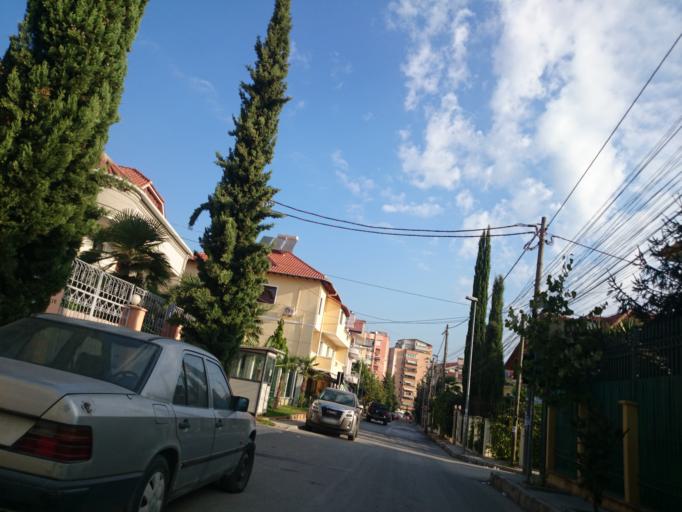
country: AL
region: Tirane
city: Tirana
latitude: 41.3163
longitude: 19.7996
